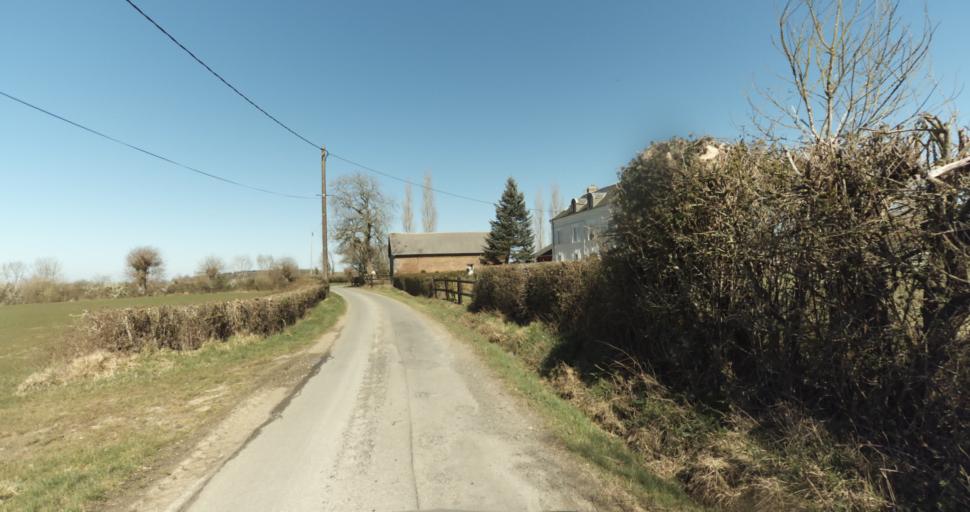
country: FR
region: Lower Normandy
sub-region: Departement du Calvados
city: Livarot
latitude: 49.0096
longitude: 0.1045
